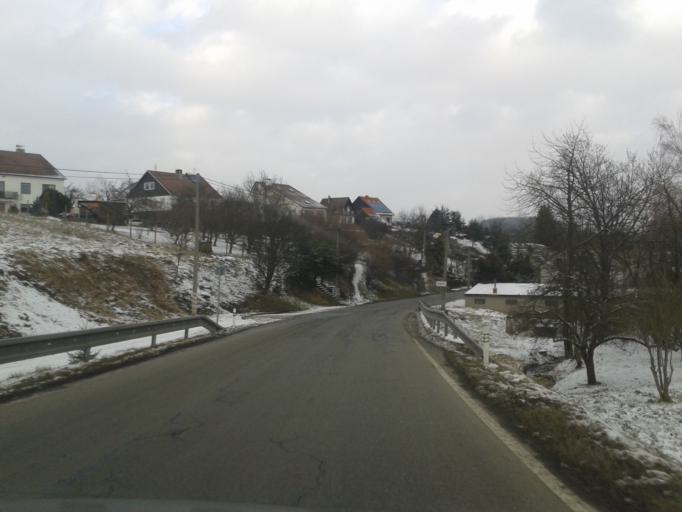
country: CZ
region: Olomoucky
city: Konice
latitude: 49.5888
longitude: 16.8781
